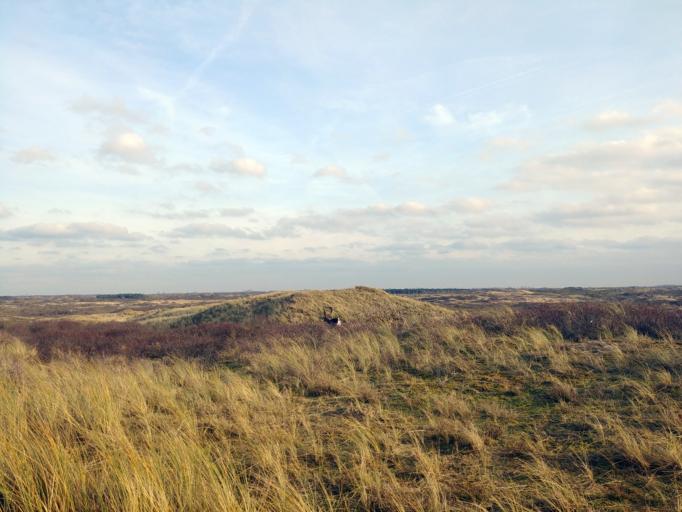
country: NL
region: South Holland
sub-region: Gemeente Noordwijkerhout
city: Noordwijkerhout
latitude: 52.3240
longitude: 4.4923
